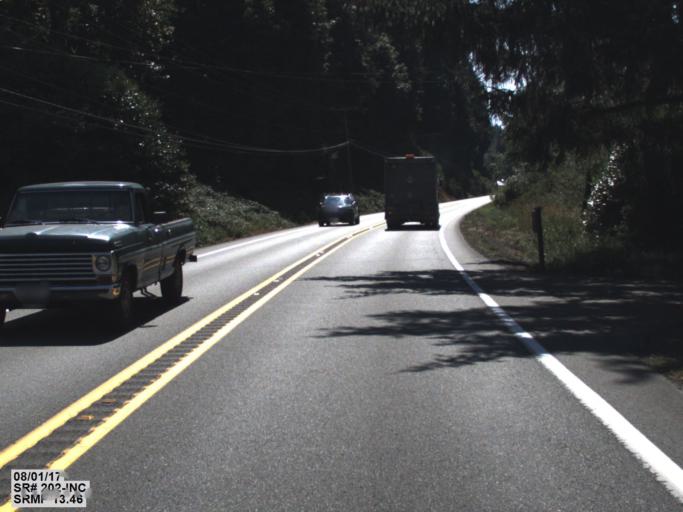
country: US
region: Washington
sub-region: King County
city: Ames Lake
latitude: 47.6360
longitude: -122.0024
